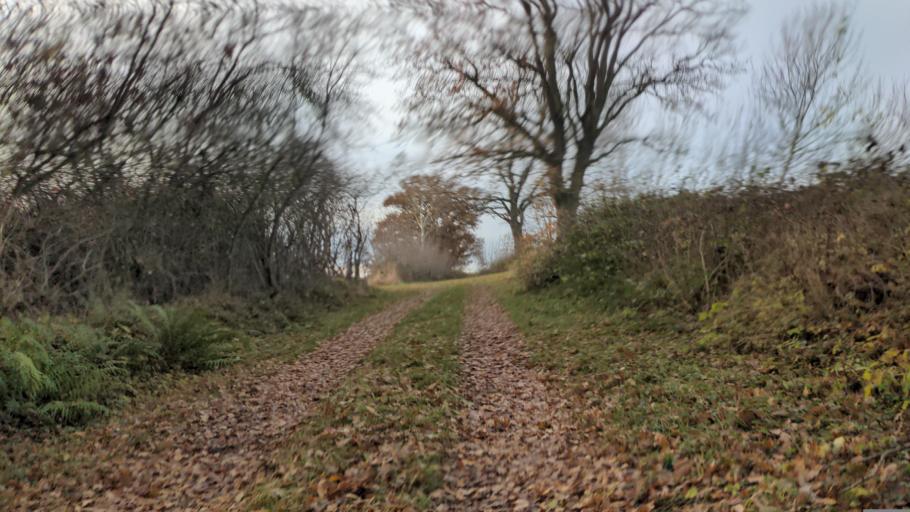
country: DE
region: Schleswig-Holstein
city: Neustadt in Holstein
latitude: 54.0880
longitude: 10.7920
